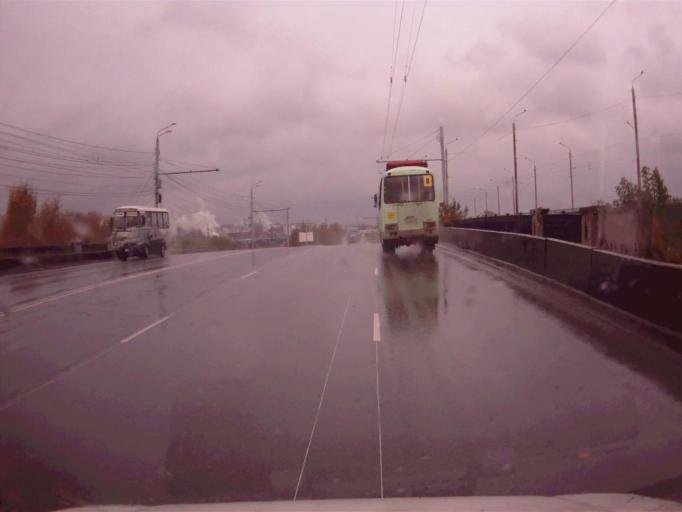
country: RU
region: Chelyabinsk
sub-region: Gorod Chelyabinsk
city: Chelyabinsk
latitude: 55.1972
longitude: 61.3861
